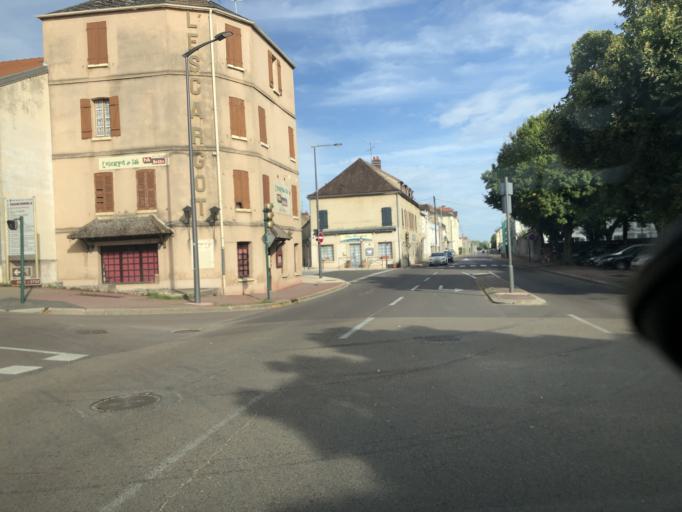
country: FR
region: Bourgogne
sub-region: Departement de l'Yonne
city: Joigny
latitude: 47.9806
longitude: 3.4007
